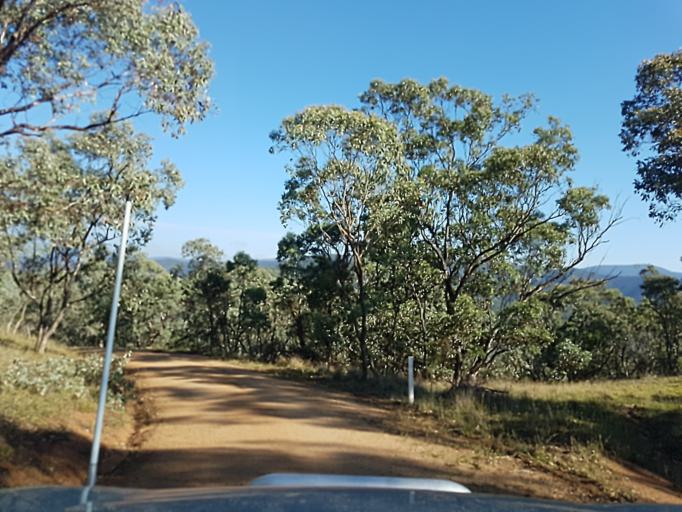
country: AU
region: New South Wales
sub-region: Snowy River
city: Jindabyne
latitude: -36.9504
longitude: 148.3516
